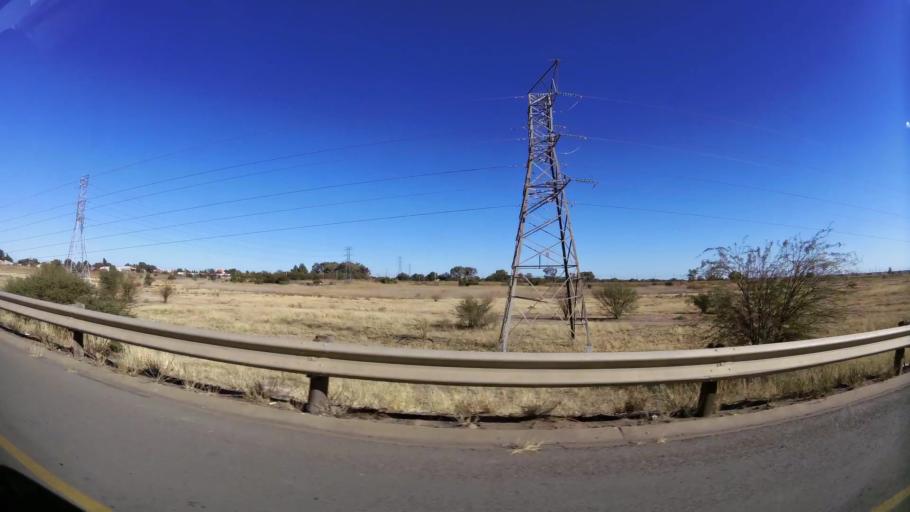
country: ZA
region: Northern Cape
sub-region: Frances Baard District Municipality
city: Kimberley
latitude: -28.7107
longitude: 24.7762
